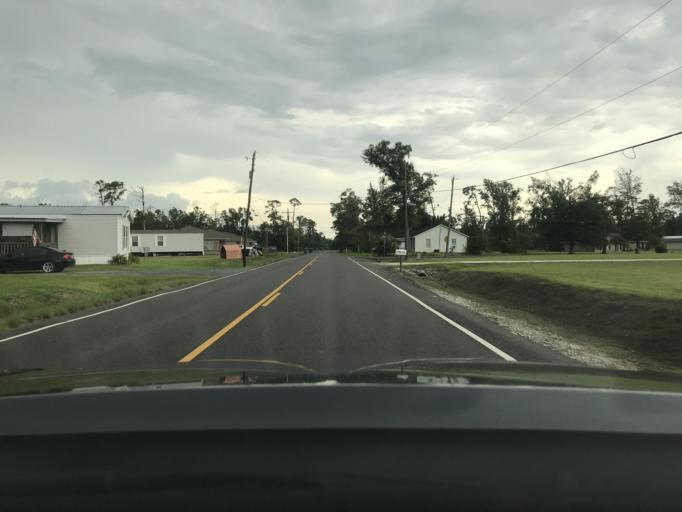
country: US
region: Louisiana
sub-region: Calcasieu Parish
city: Westlake
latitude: 30.2720
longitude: -93.2410
